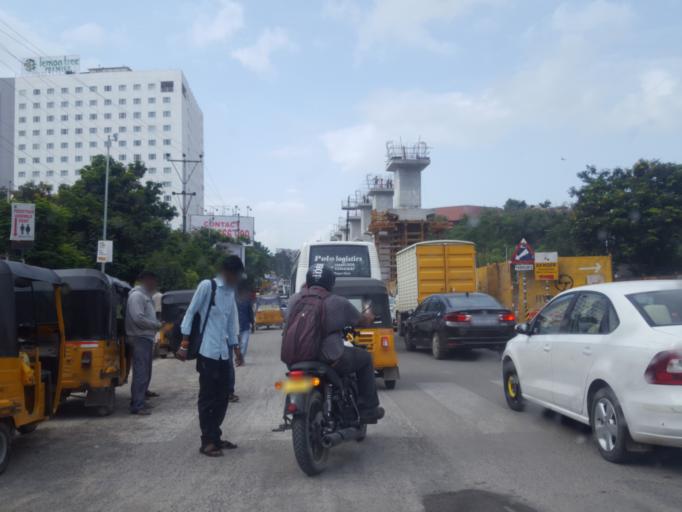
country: IN
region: Telangana
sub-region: Rangareddi
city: Kukatpalli
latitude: 17.4414
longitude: 78.3771
